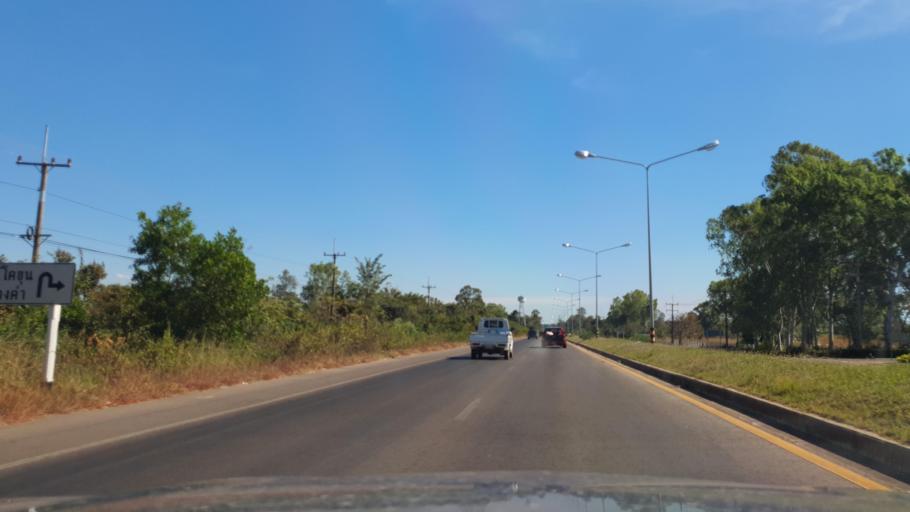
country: TH
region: Sakon Nakhon
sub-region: Amphoe Khok Si Suphan
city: Khok Si Suphan
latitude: 17.0765
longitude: 104.2028
